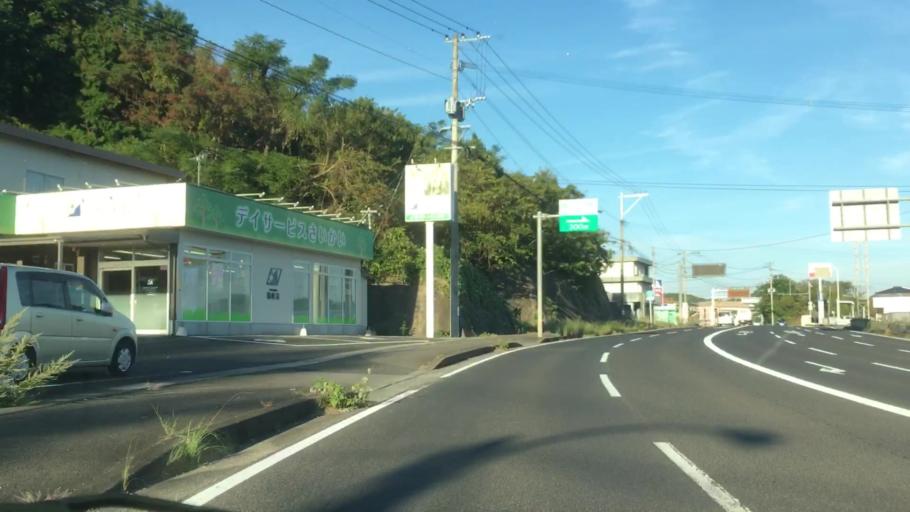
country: JP
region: Nagasaki
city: Sasebo
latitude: 33.0435
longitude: 129.7421
